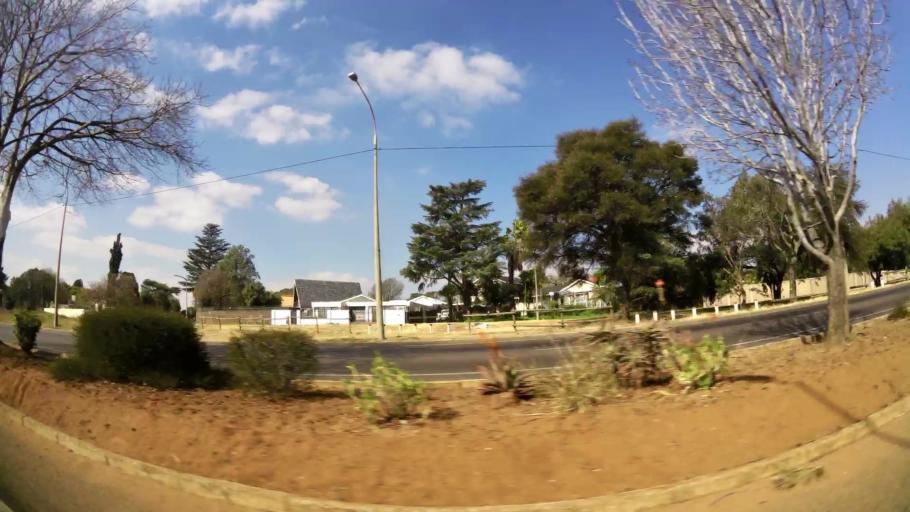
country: ZA
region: Gauteng
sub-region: West Rand District Municipality
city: Krugersdorp
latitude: -26.0841
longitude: 27.7887
